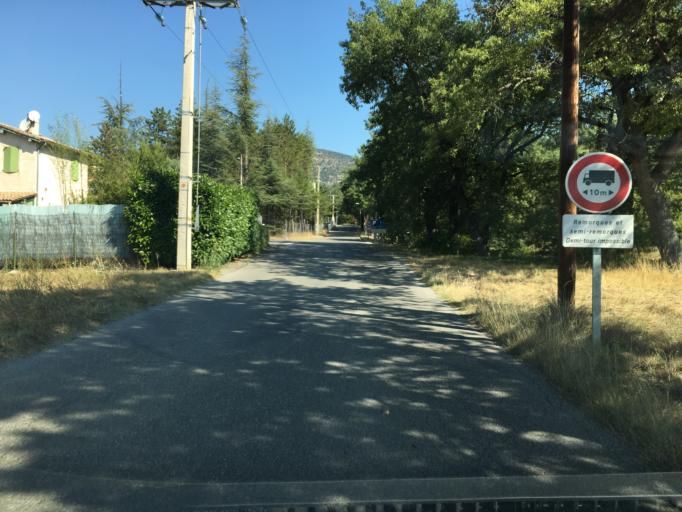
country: FR
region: Provence-Alpes-Cote d'Azur
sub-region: Departement des Alpes-de-Haute-Provence
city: Mallemoisson
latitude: 44.0571
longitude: 6.1492
